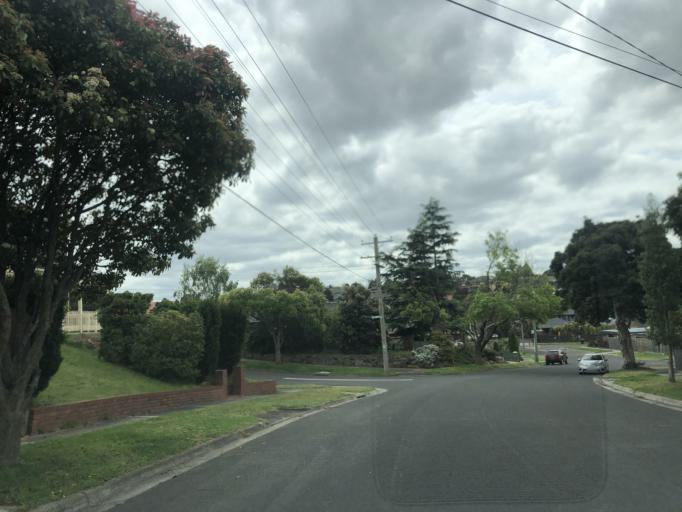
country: AU
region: Victoria
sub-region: Greater Dandenong
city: Dandenong North
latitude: -37.9480
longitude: 145.2128
